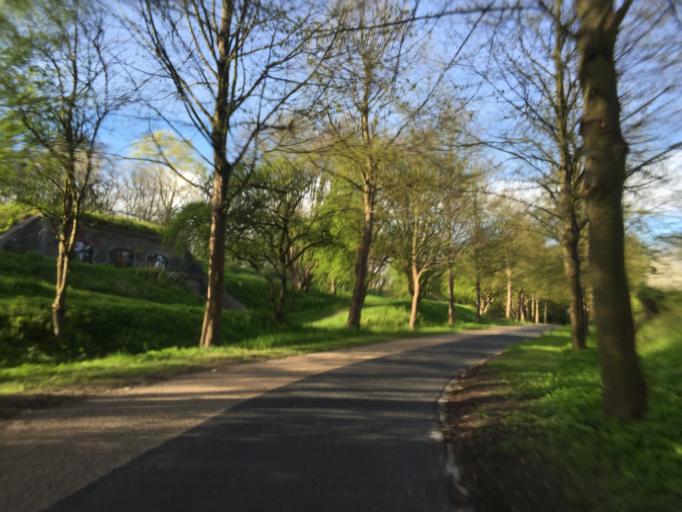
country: DK
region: Capital Region
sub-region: Herlev Kommune
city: Herlev
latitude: 55.7122
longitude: 12.4634
